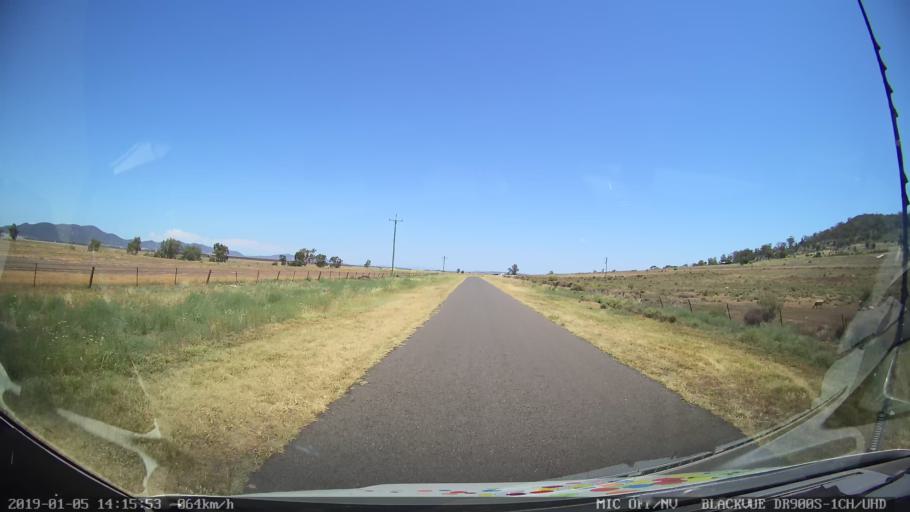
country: AU
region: New South Wales
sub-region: Liverpool Plains
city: Quirindi
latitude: -31.2513
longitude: 150.4718
